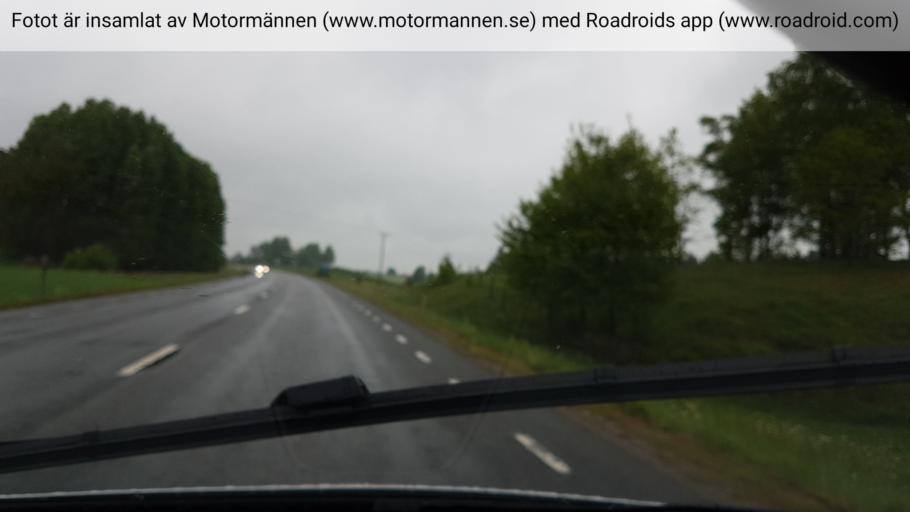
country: SE
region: Vaestra Goetaland
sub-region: Falkopings Kommun
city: Falkoeping
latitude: 57.9702
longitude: 13.5299
